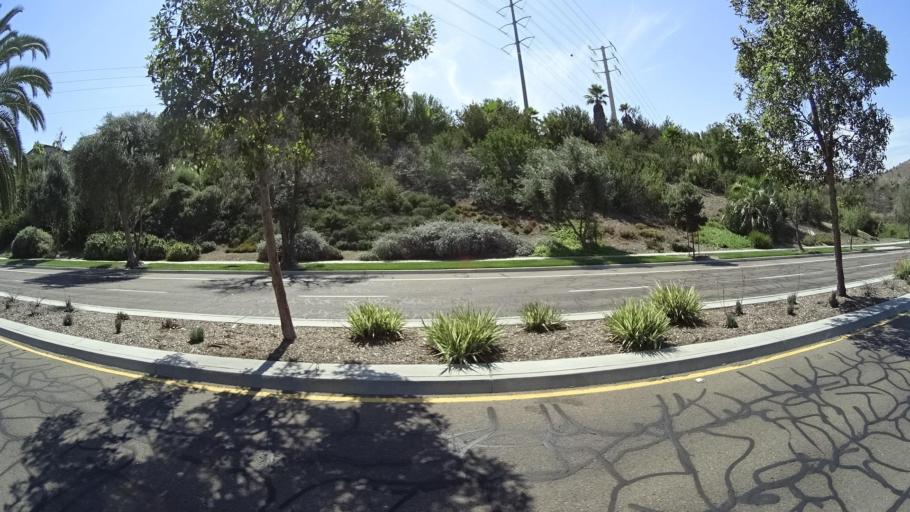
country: US
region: California
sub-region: San Diego County
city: La Presa
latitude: 32.6707
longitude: -116.9826
